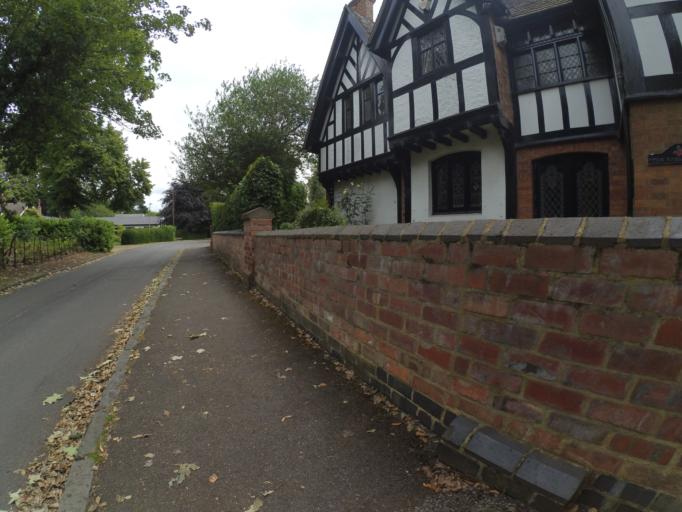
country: GB
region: England
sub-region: Warwickshire
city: Dunchurch
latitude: 52.3607
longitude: -1.2886
